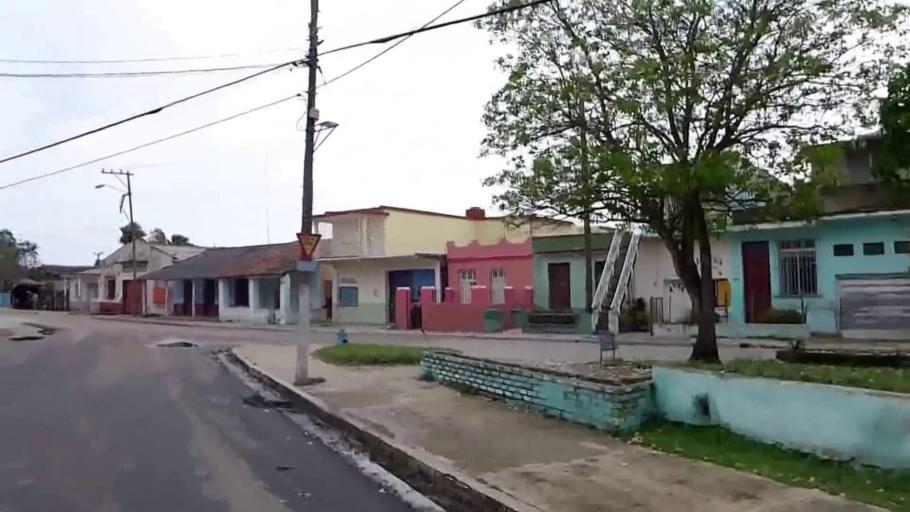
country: CU
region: Camaguey
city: Camaguey
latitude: 21.3866
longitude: -77.9332
